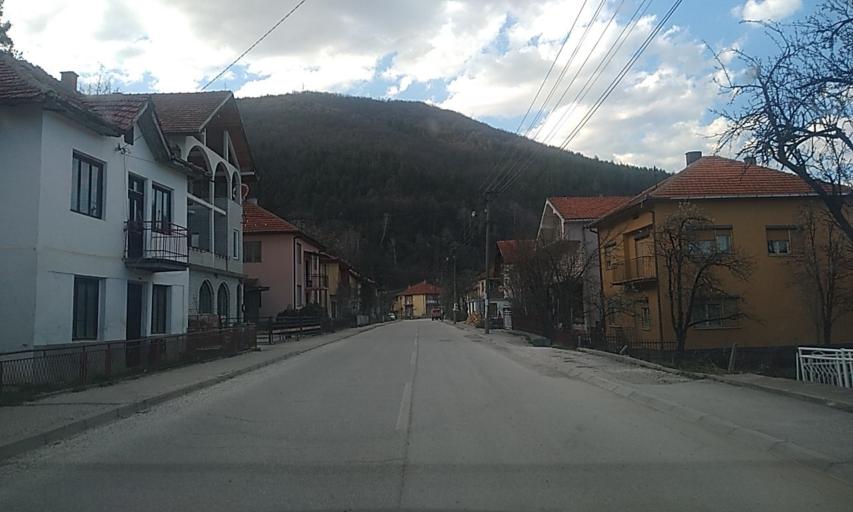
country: RS
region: Central Serbia
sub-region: Pcinjski Okrug
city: Bosilegrad
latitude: 42.4971
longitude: 22.4694
